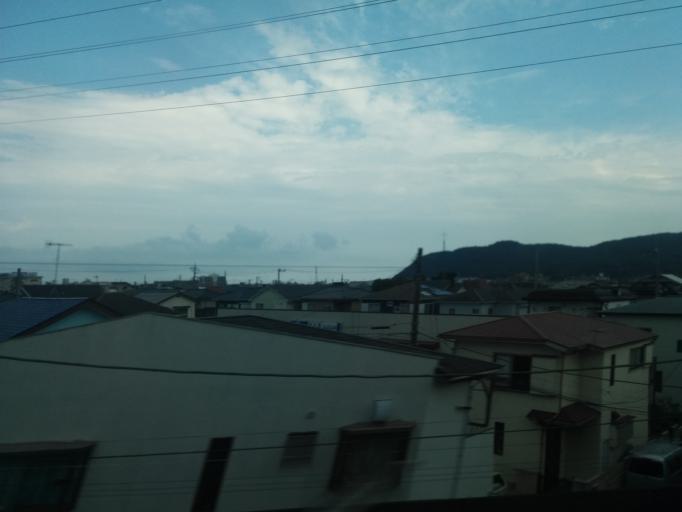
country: JP
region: Kanagawa
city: Hiratsuka
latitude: 35.3431
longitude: 139.3083
